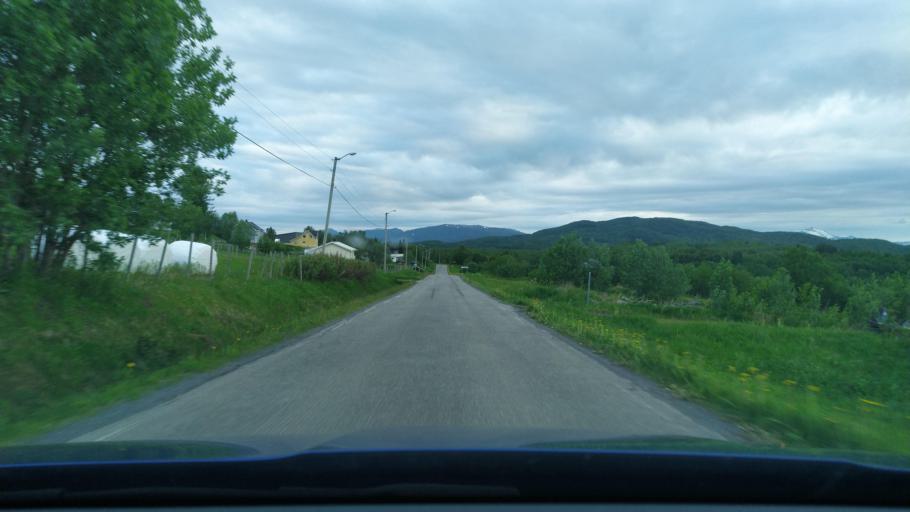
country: NO
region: Troms
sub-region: Tranoy
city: Vangsvika
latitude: 69.1137
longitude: 17.7919
